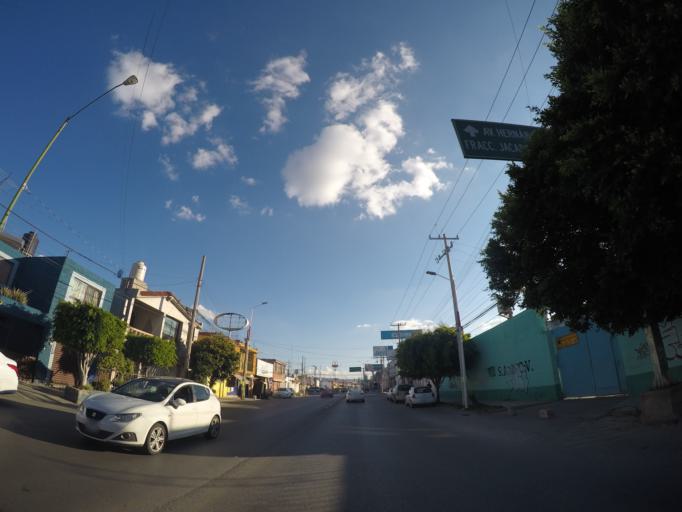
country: MX
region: San Luis Potosi
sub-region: San Luis Potosi
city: San Luis Potosi
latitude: 22.1721
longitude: -101.0006
